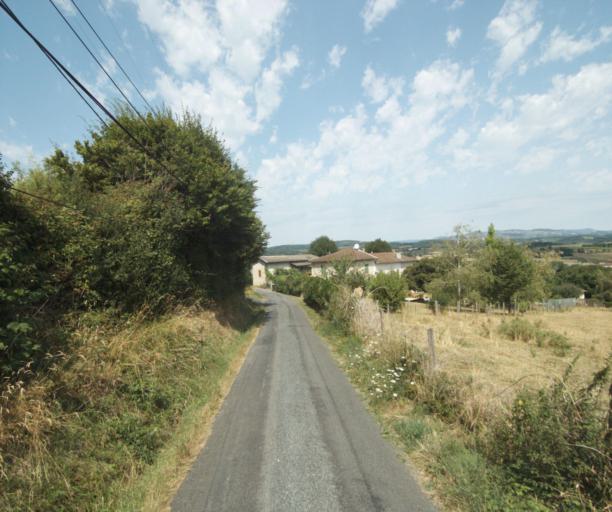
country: FR
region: Rhone-Alpes
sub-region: Departement du Rhone
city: Lentilly
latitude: 45.8456
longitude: 4.6533
